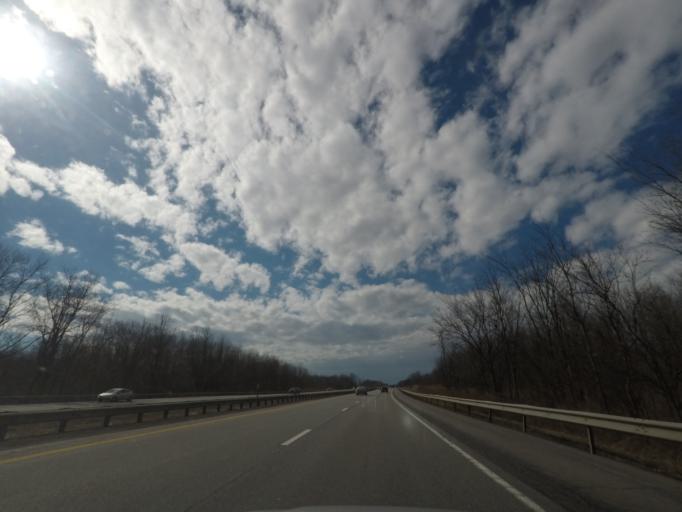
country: US
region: New York
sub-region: Madison County
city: Canastota
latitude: 43.0902
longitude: -75.7642
